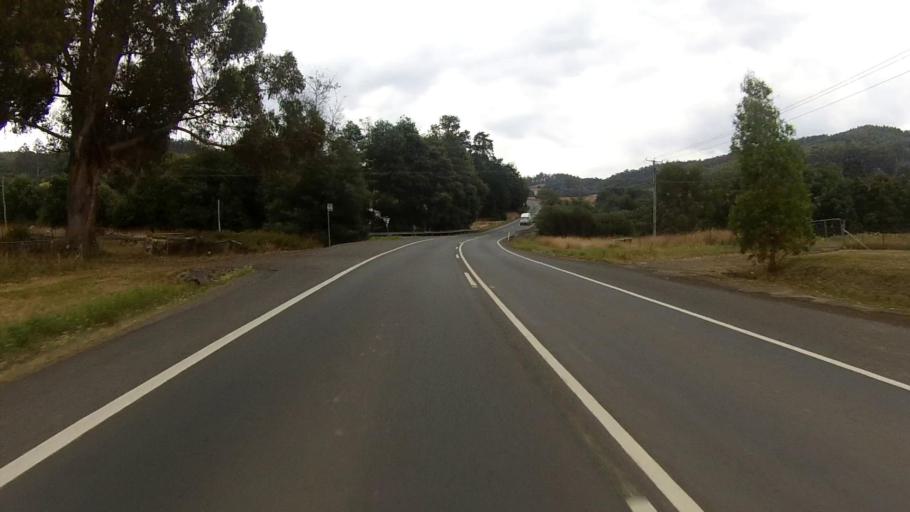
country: AU
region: Tasmania
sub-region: Huon Valley
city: Cygnet
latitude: -43.1370
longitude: 147.0552
